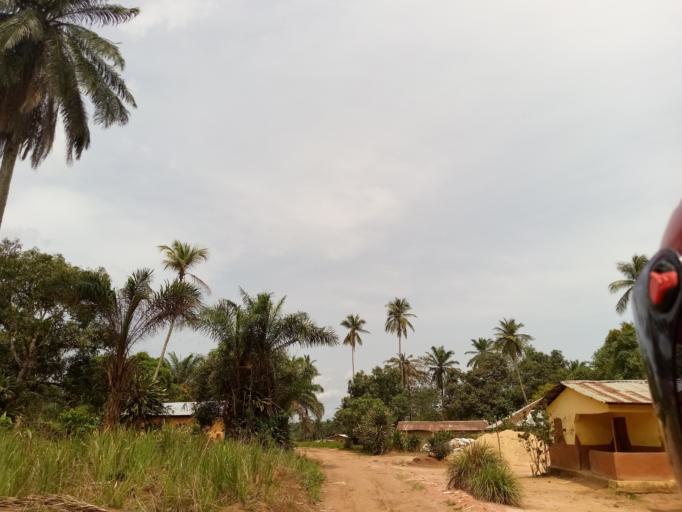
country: SL
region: Western Area
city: Waterloo
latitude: 8.3248
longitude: -13.0128
